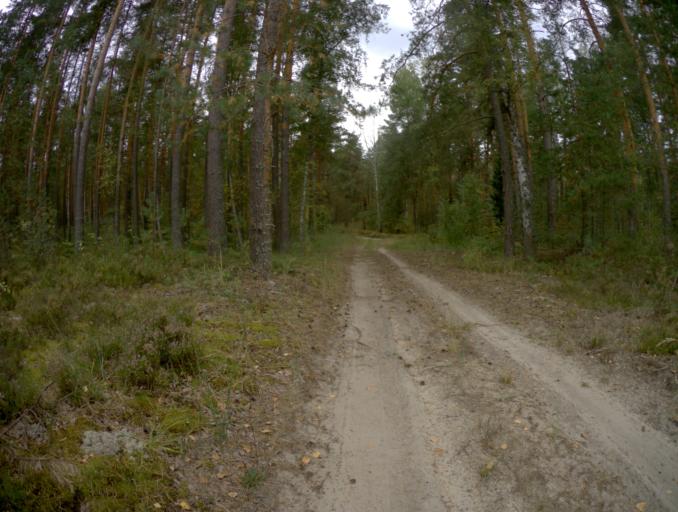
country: RU
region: Vladimir
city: Ivanishchi
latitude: 55.8351
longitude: 40.3180
